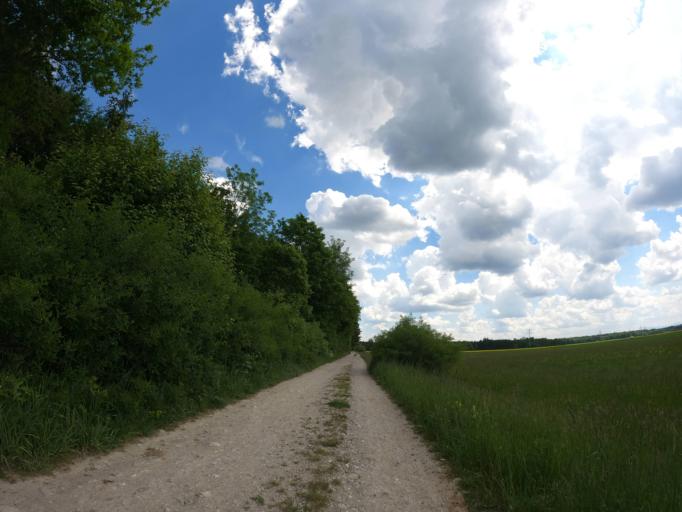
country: DE
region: Bavaria
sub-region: Upper Bavaria
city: Sauerlach
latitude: 47.9846
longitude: 11.6648
